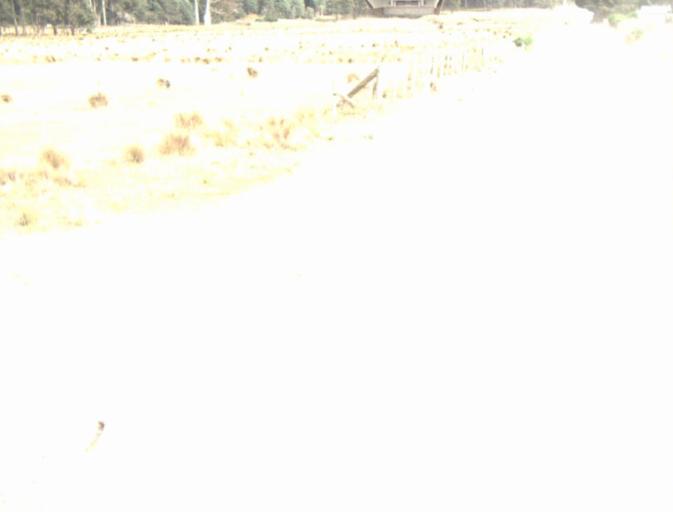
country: AU
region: Tasmania
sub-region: Dorset
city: Scottsdale
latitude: -41.3697
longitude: 147.4702
